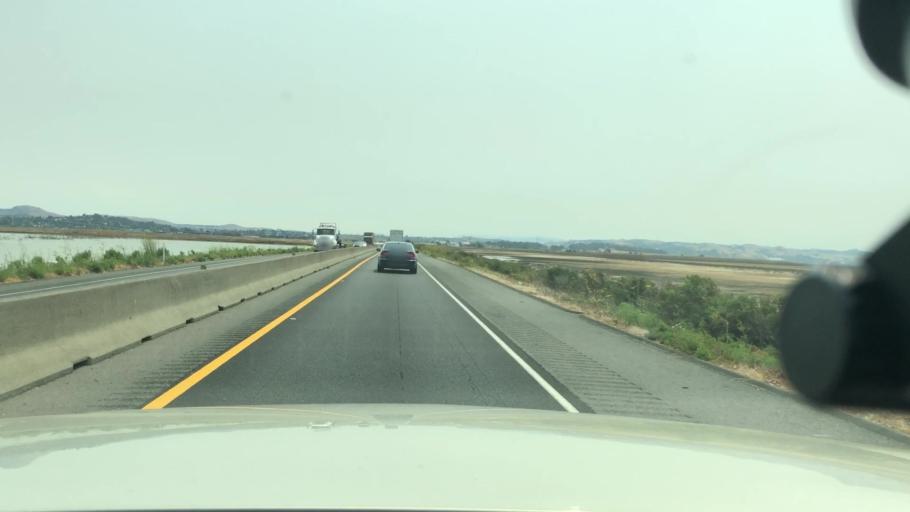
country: US
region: California
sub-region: Solano County
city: Vallejo
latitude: 38.1241
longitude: -122.3180
